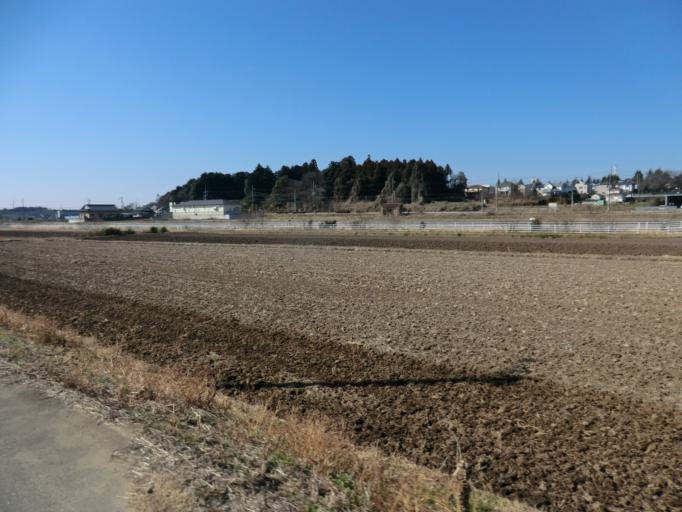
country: JP
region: Ibaraki
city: Naka
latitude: 36.0647
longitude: 140.0840
